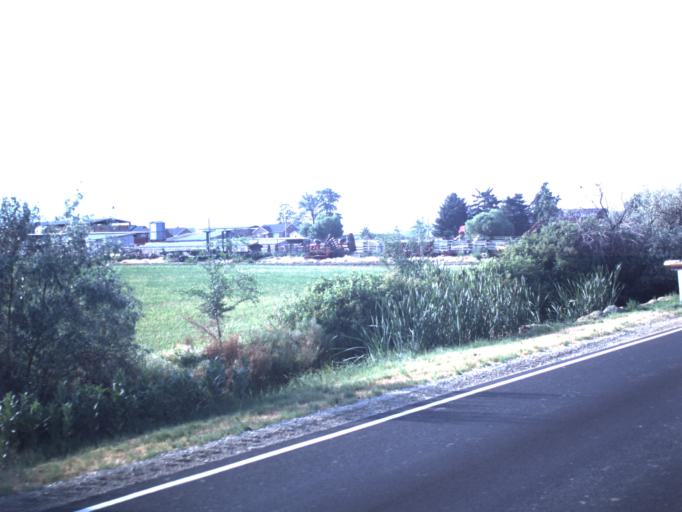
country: US
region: Utah
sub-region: Weber County
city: Plain City
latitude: 41.2586
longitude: -112.0925
